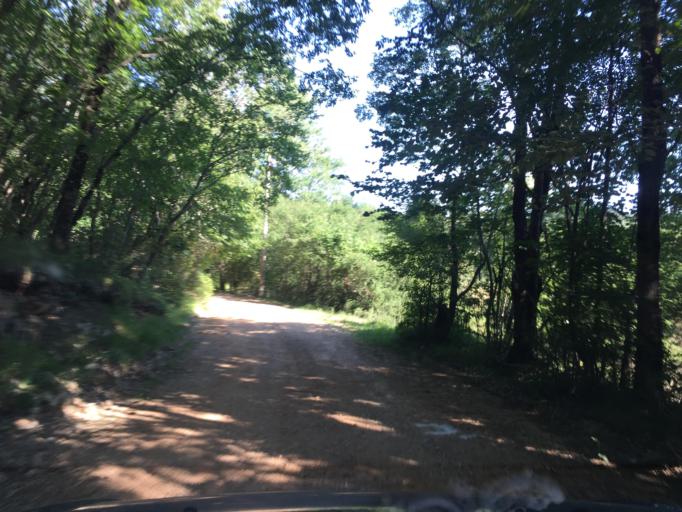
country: HR
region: Primorsko-Goranska
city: Klana
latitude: 45.4418
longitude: 14.4087
